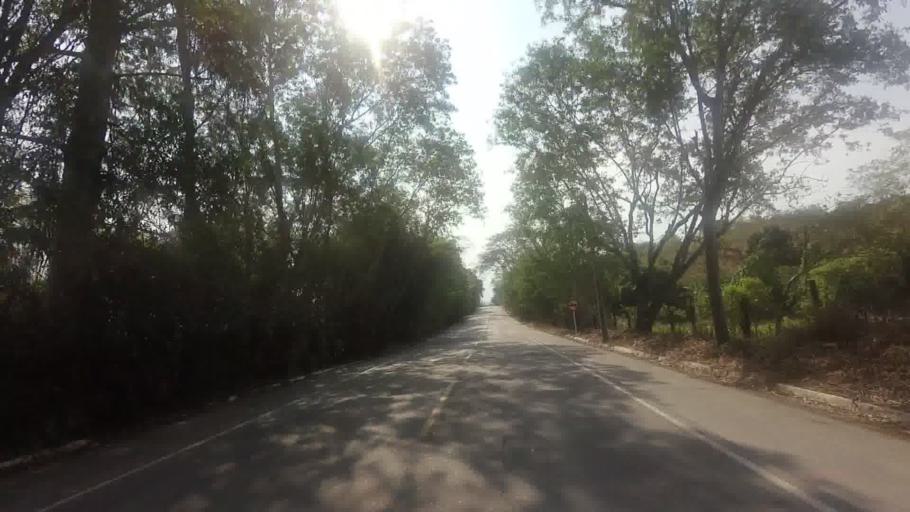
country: BR
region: Rio de Janeiro
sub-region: Bom Jesus Do Itabapoana
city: Bom Jesus do Itabapoana
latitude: -21.1494
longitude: -41.6171
